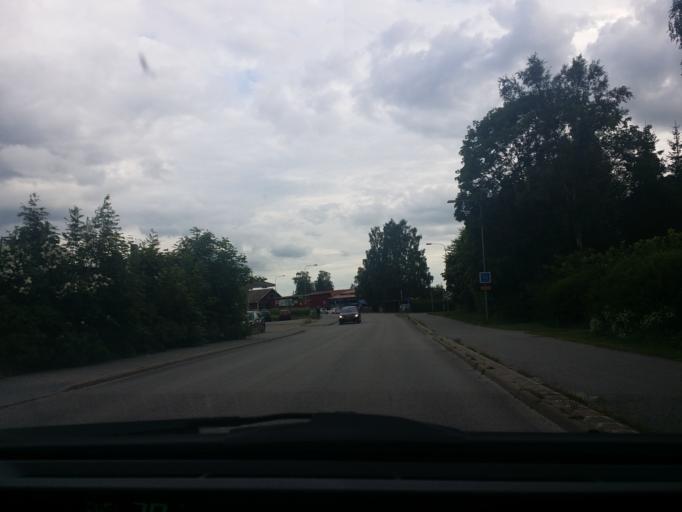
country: SE
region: OErebro
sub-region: Nora Kommun
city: Nora
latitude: 59.5254
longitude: 15.0353
